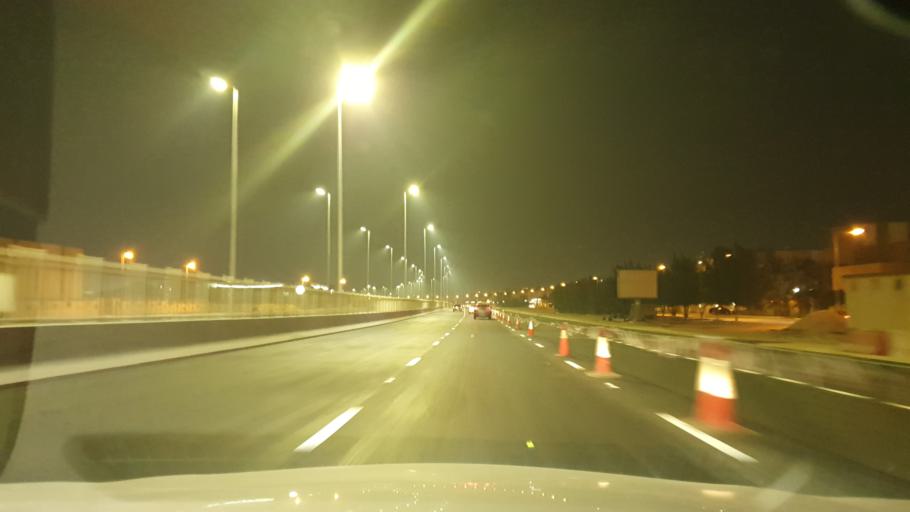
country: BH
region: Northern
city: Madinat `Isa
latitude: 26.1573
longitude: 50.5497
